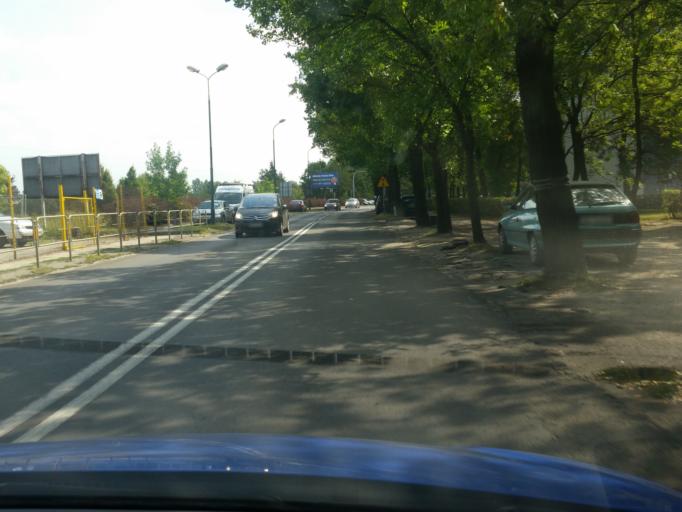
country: PL
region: Silesian Voivodeship
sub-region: Sosnowiec
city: Sosnowiec
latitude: 50.2682
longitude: 19.1362
